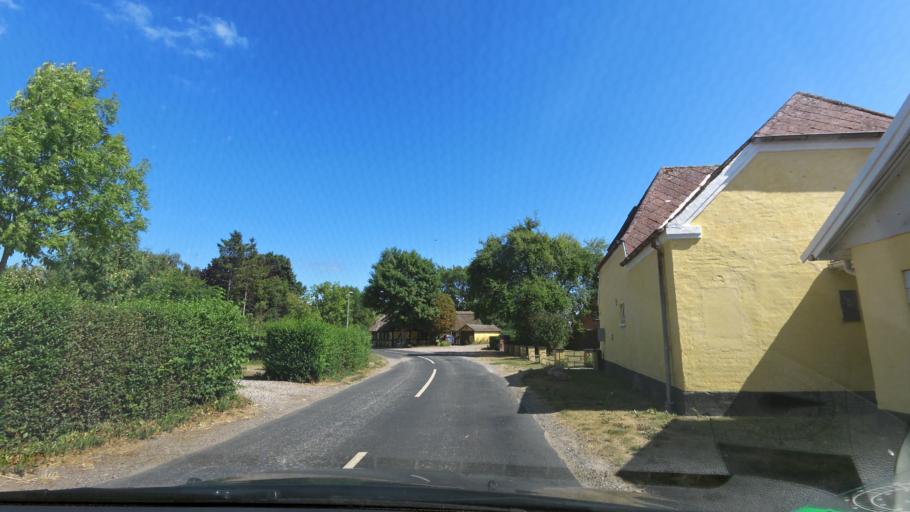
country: DK
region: South Denmark
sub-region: Nordfyns Kommune
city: Otterup
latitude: 55.5494
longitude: 10.4665
